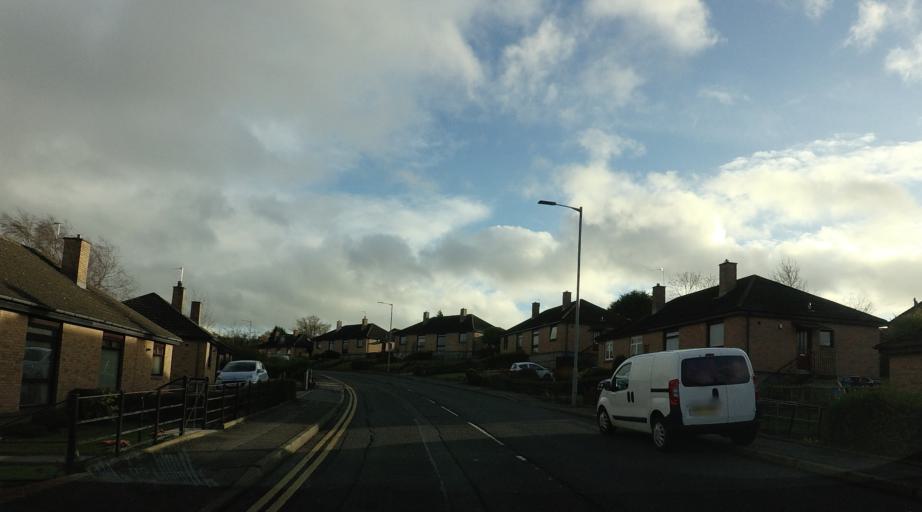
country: GB
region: Scotland
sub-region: Falkirk
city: Polmont
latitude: 55.9757
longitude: -3.7115
